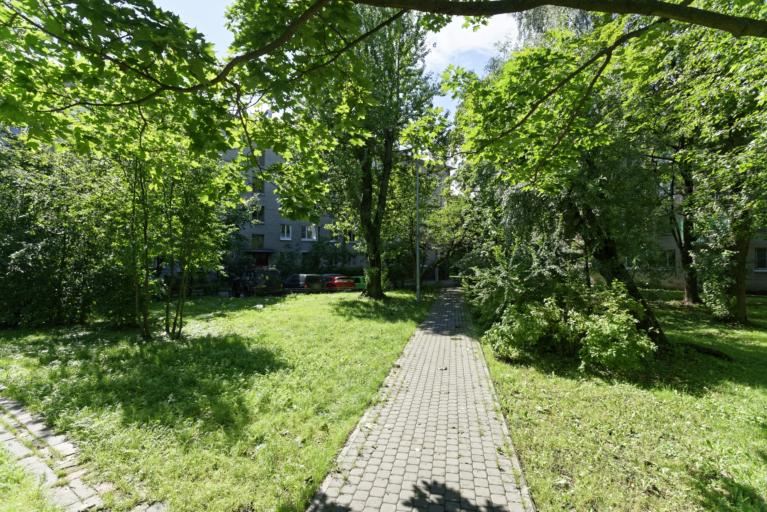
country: RU
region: St.-Petersburg
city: Vasyl'evsky Ostrov
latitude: 59.9435
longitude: 30.2369
